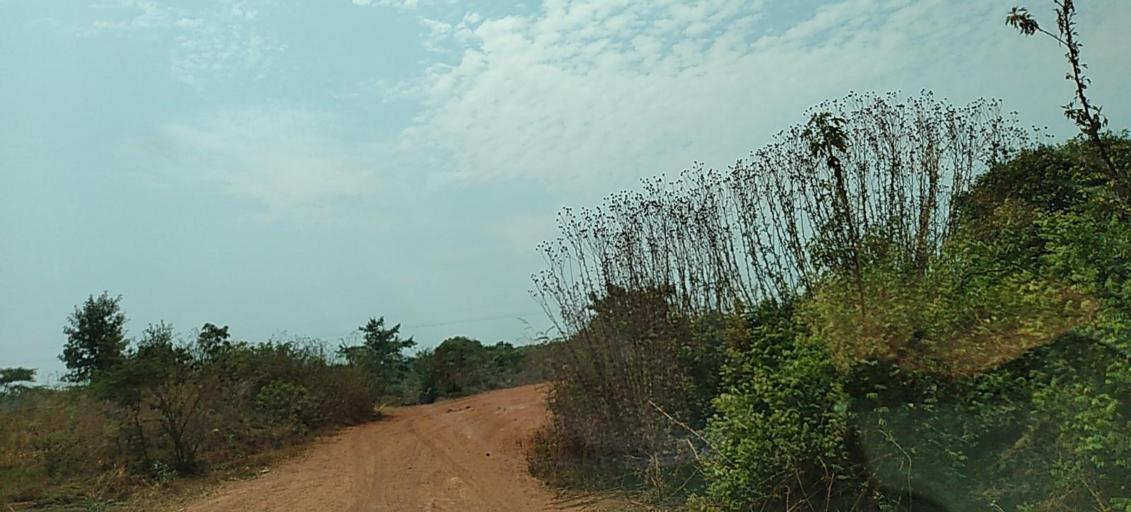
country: ZM
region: Copperbelt
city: Kalulushi
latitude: -12.8933
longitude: 28.0797
